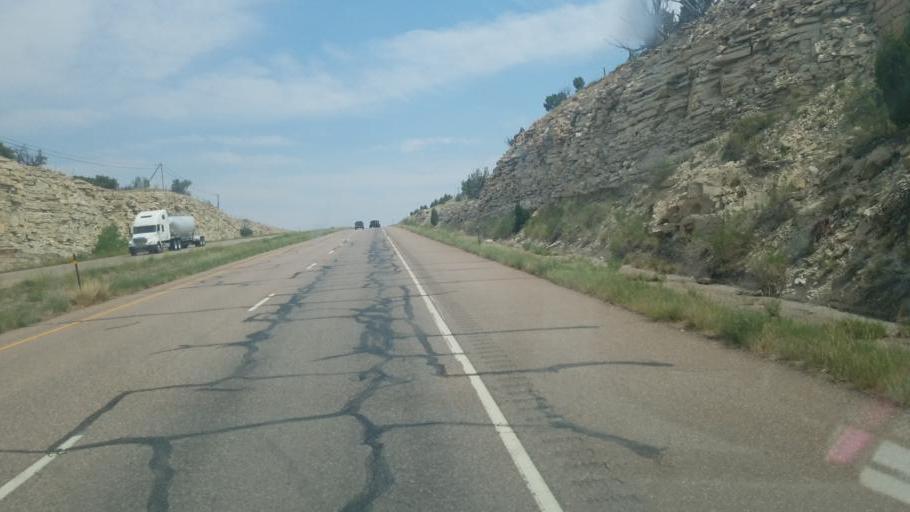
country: US
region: Colorado
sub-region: Fremont County
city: Penrose
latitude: 38.3761
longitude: -104.9474
